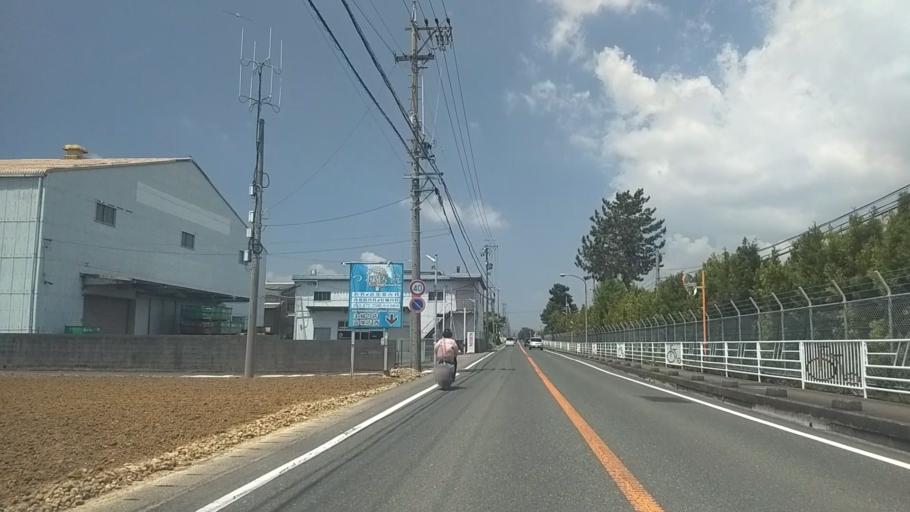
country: JP
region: Shizuoka
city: Hamamatsu
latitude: 34.7417
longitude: 137.6939
